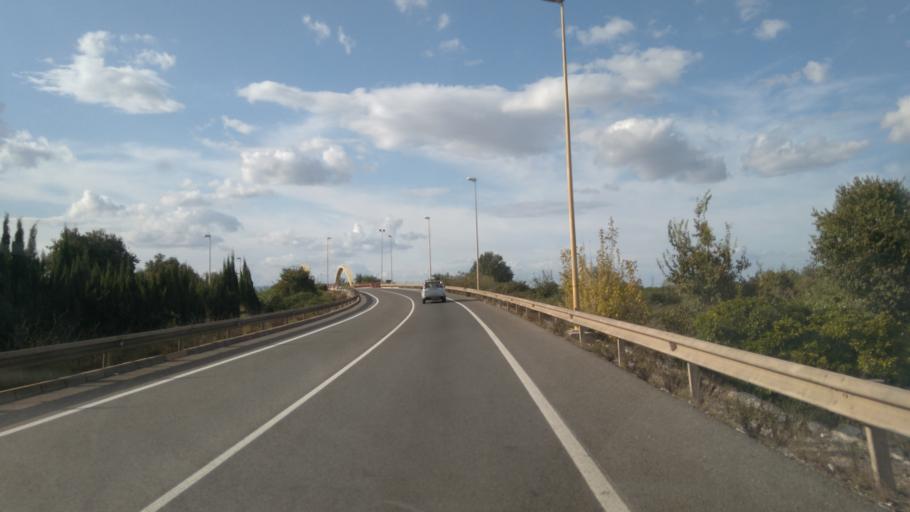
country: ES
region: Valencia
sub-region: Provincia de Valencia
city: Alzira
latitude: 39.1616
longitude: -0.4339
